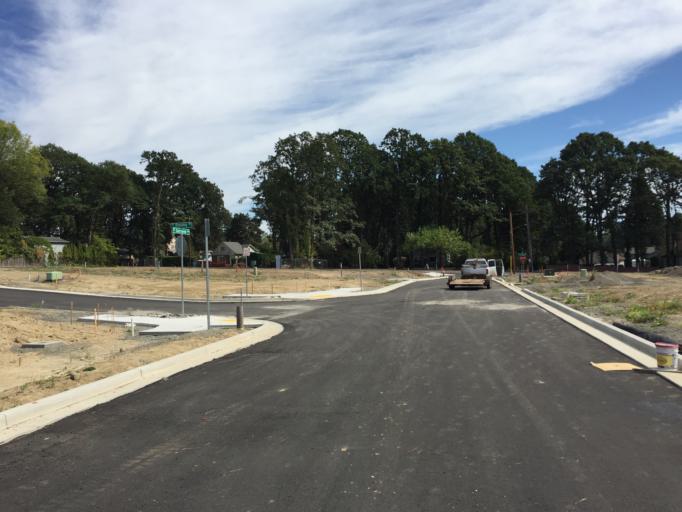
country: US
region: Oregon
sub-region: Clackamas County
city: Oak Grove
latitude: 45.4085
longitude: -122.6310
